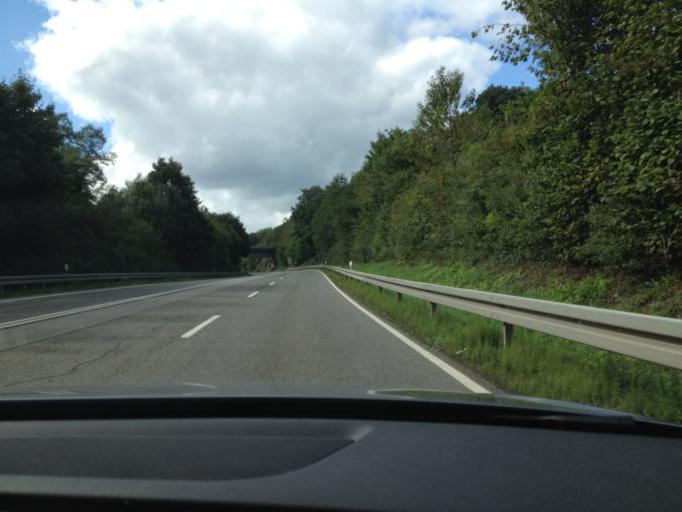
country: DE
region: Saarland
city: Namborn
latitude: 49.5147
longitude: 7.1533
